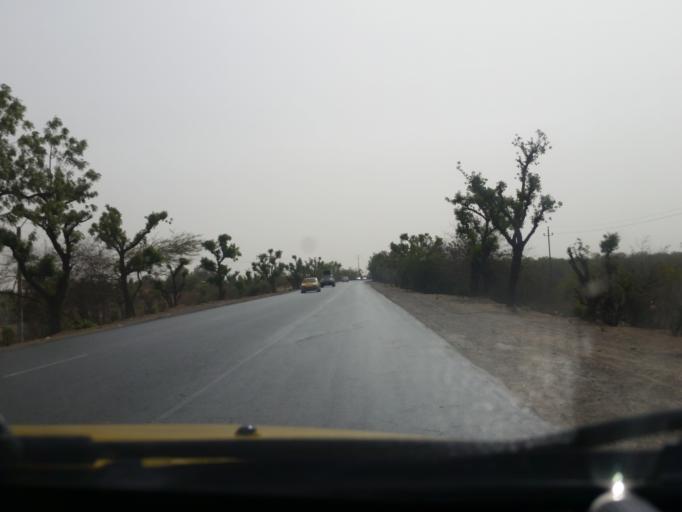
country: SN
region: Thies
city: Thies Nones
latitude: 14.7813
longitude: -16.9823
